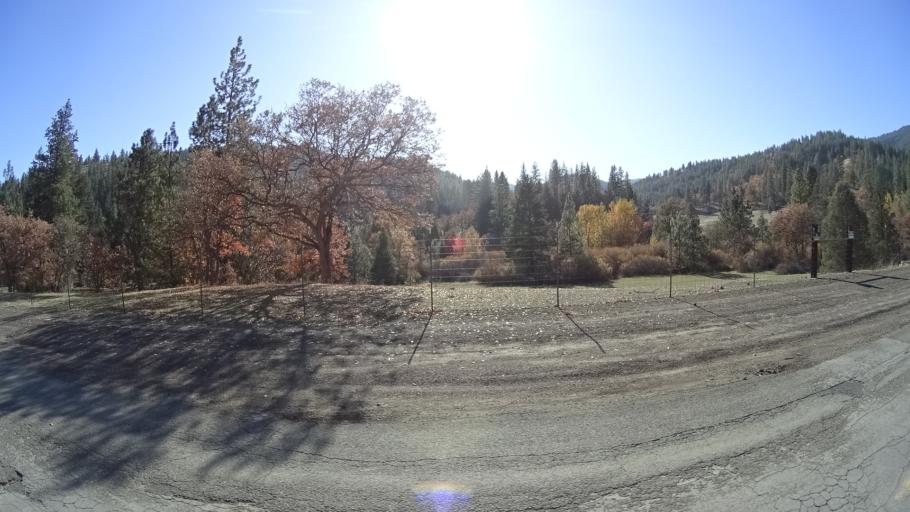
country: US
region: California
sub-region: Siskiyou County
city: Yreka
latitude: 41.7202
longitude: -122.6876
